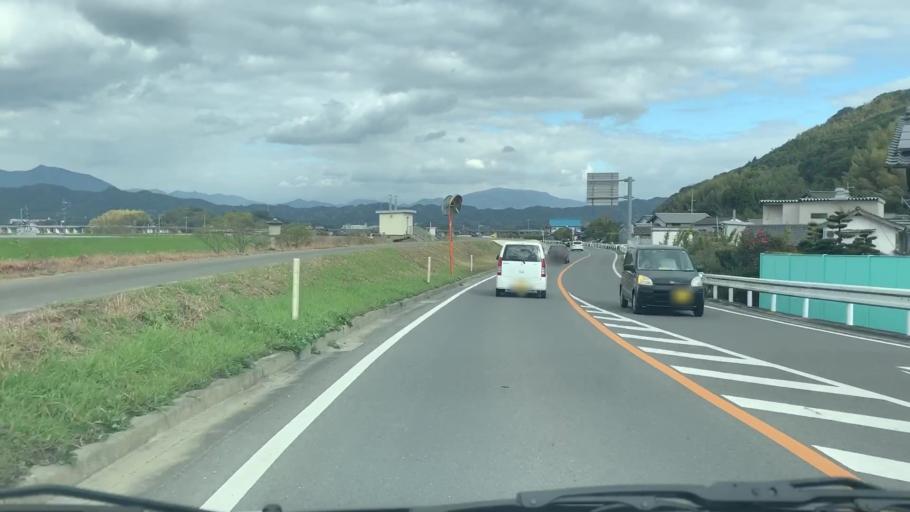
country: JP
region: Saga Prefecture
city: Takeocho-takeo
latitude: 33.2025
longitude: 130.0537
